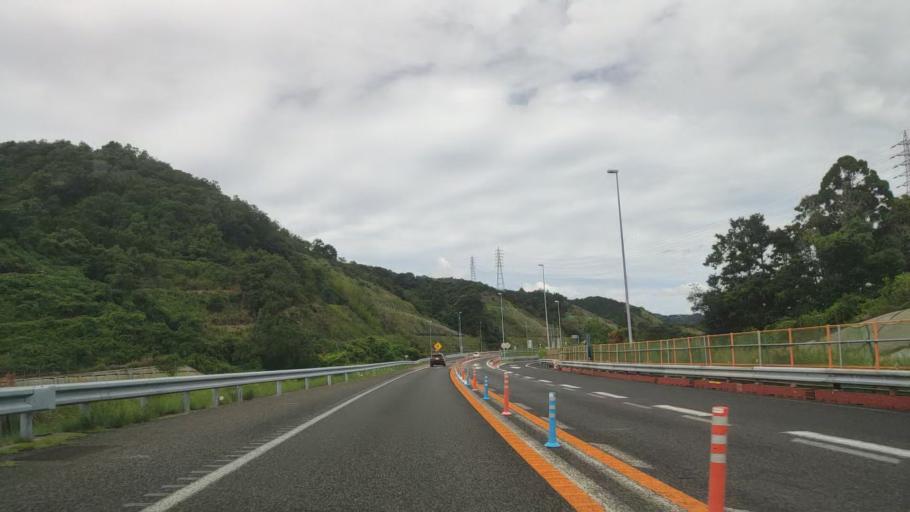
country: JP
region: Wakayama
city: Gobo
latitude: 33.8255
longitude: 135.2199
